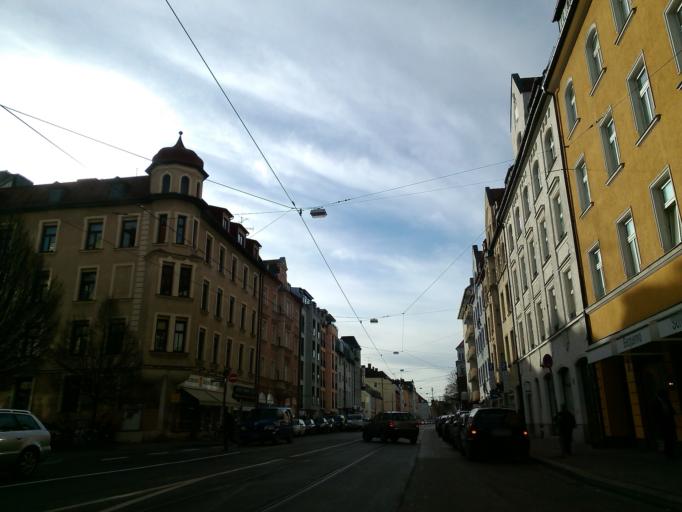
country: DE
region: Bavaria
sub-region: Upper Bavaria
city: Munich
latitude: 48.1184
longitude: 11.5828
